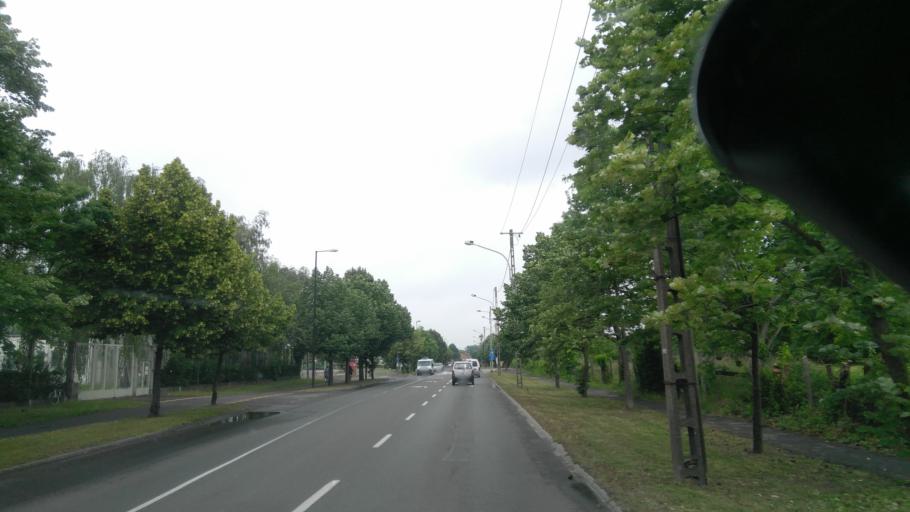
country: HU
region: Bekes
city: Bekescsaba
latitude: 46.6699
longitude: 21.1093
